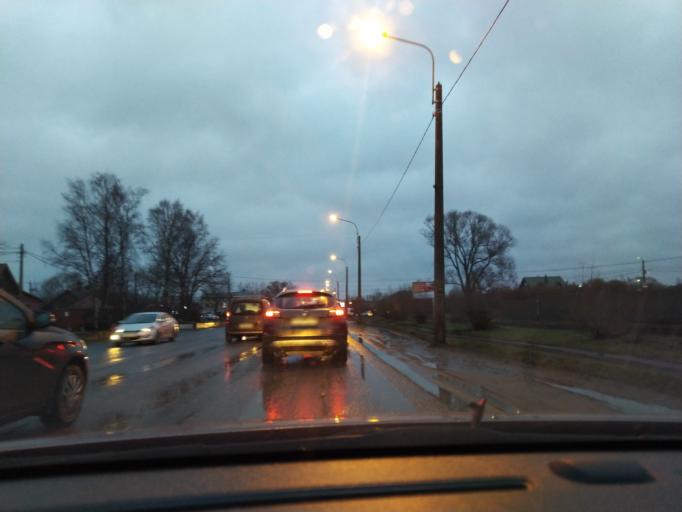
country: RU
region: St.-Petersburg
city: Uritsk
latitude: 59.8175
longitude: 30.1776
